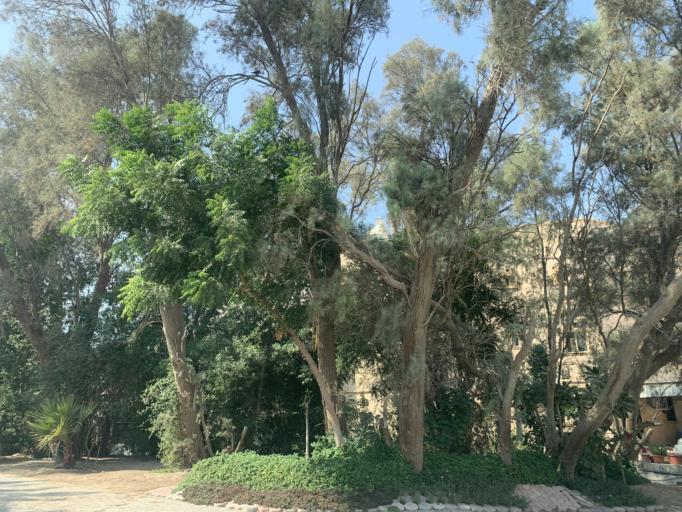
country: BH
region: Central Governorate
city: Madinat Hamad
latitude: 26.1240
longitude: 50.4920
